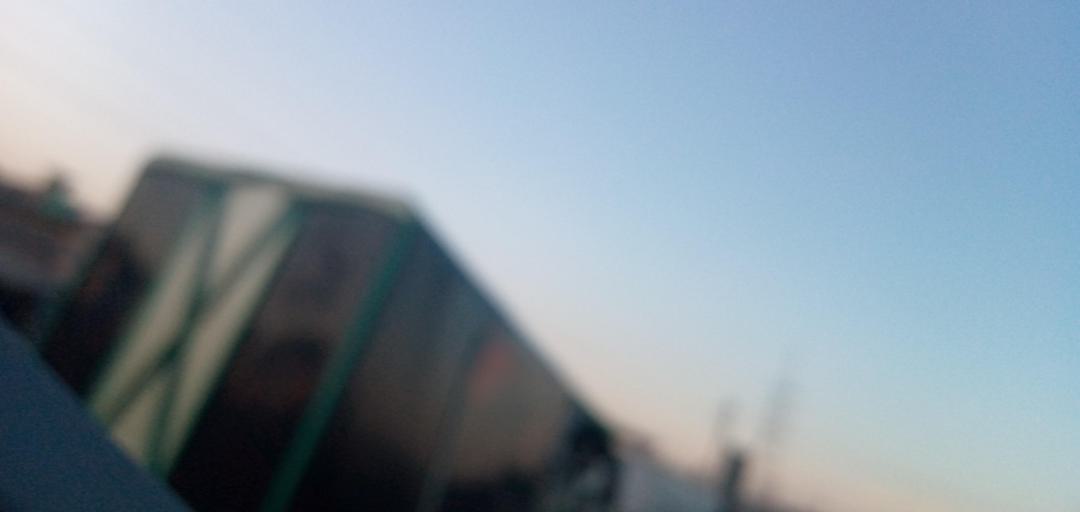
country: PK
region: Khyber Pakhtunkhwa
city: Peshawar
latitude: 34.0215
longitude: 71.6215
